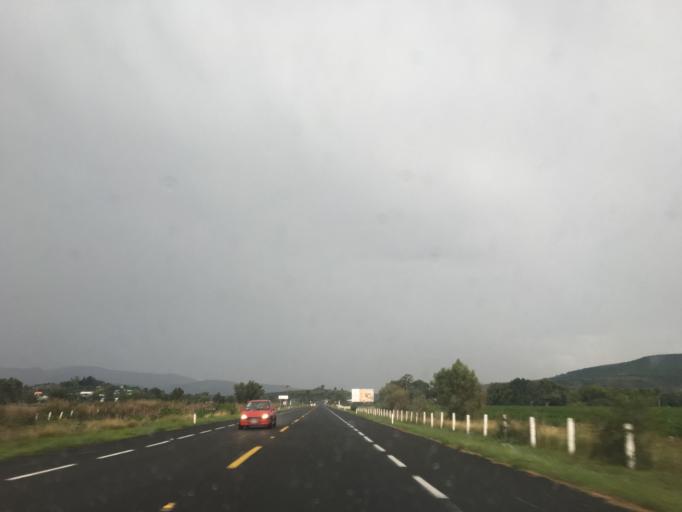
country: MX
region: Michoacan
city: Alvaro Obregon
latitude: 19.8282
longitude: -101.0110
